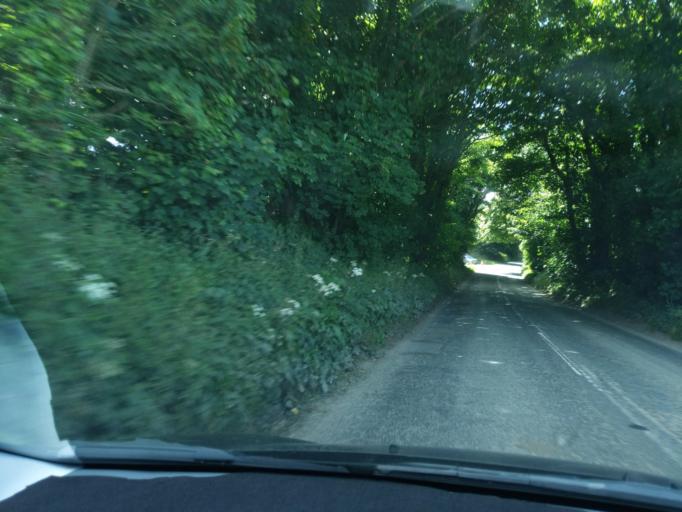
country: GB
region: England
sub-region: Cornwall
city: Perranporth
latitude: 50.2977
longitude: -5.1409
